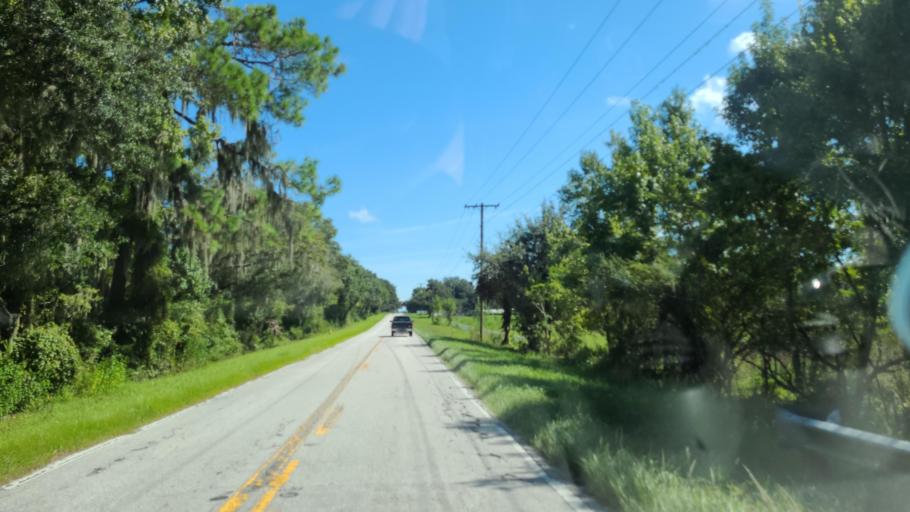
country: US
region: Florida
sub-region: Hillsborough County
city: Boyette
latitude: 27.8036
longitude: -82.2410
